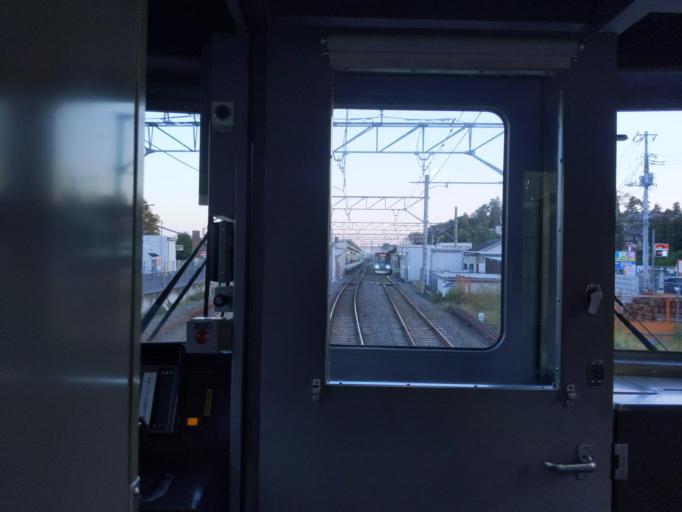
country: JP
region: Chiba
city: Noda
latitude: 35.9599
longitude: 139.8595
